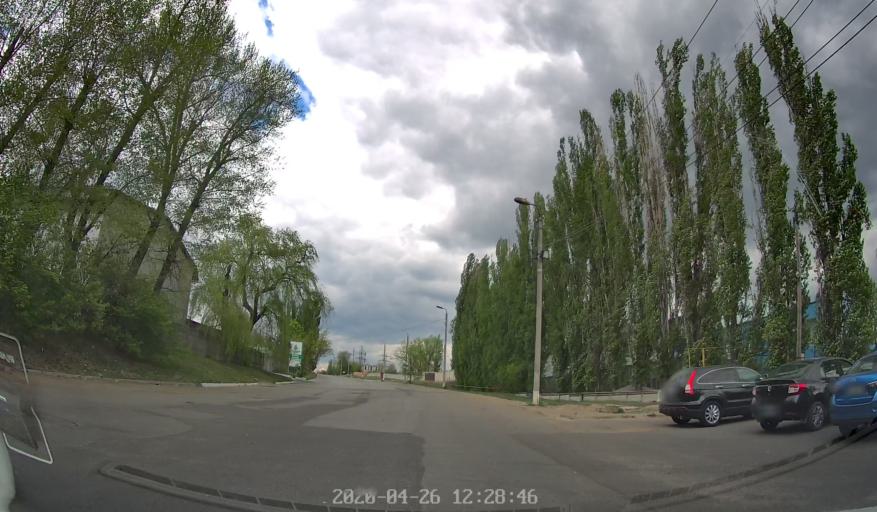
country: MD
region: Chisinau
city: Chisinau
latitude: 46.9987
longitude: 28.9066
